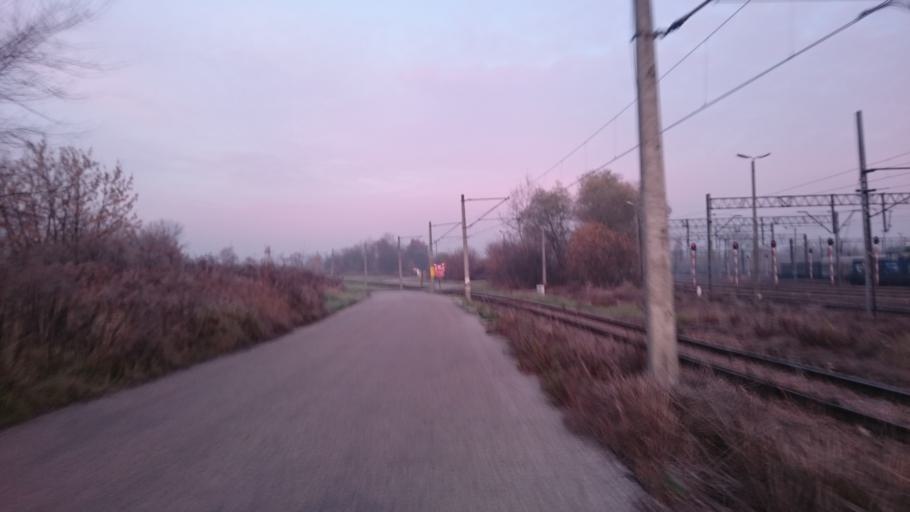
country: PL
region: Lesser Poland Voivodeship
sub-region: Powiat wielicki
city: Czarnochowice
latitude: 50.0276
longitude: 20.0050
